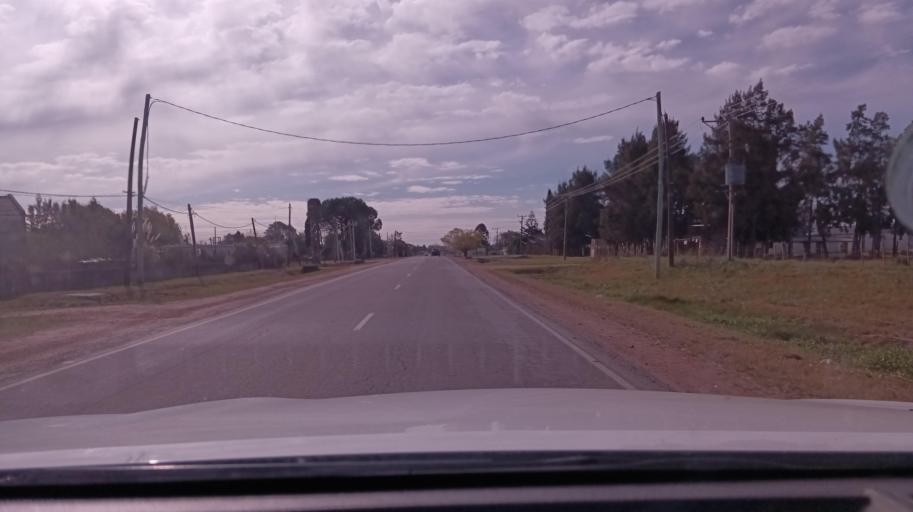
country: UY
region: Canelones
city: Toledo
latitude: -34.7229
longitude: -56.1131
